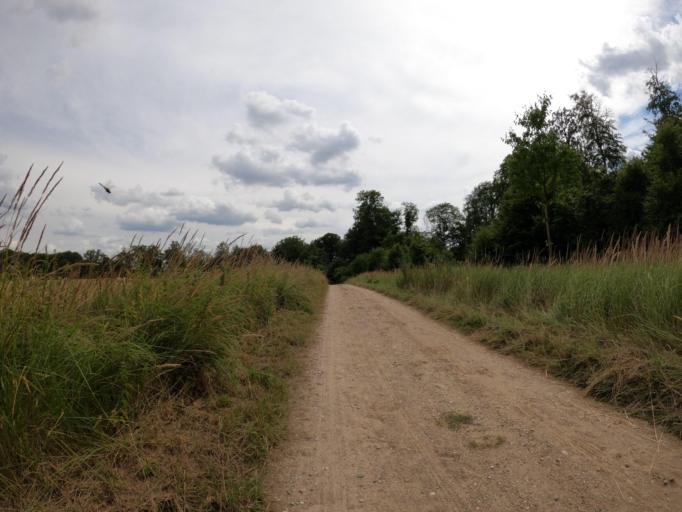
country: DE
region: Mecklenburg-Vorpommern
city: Loitz
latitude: 53.3570
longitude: 13.4362
